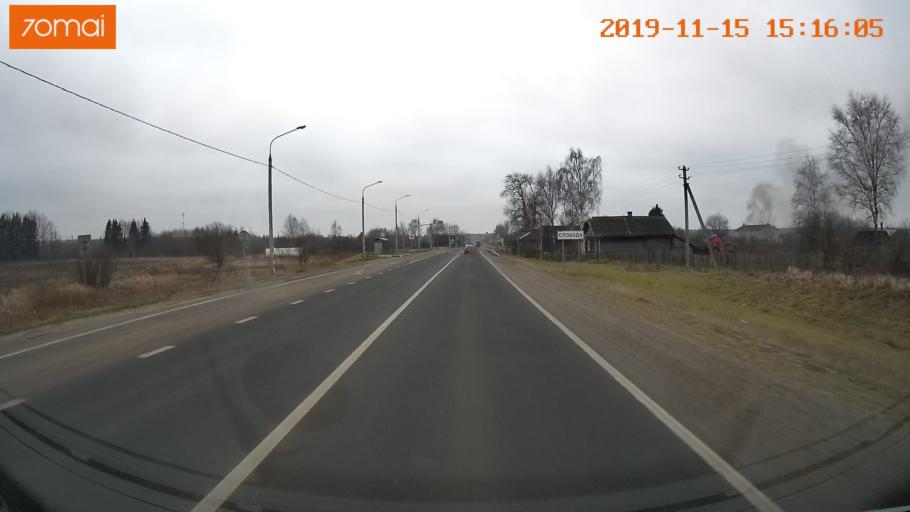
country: RU
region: Jaroslavl
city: Danilov
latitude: 58.2761
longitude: 40.1943
